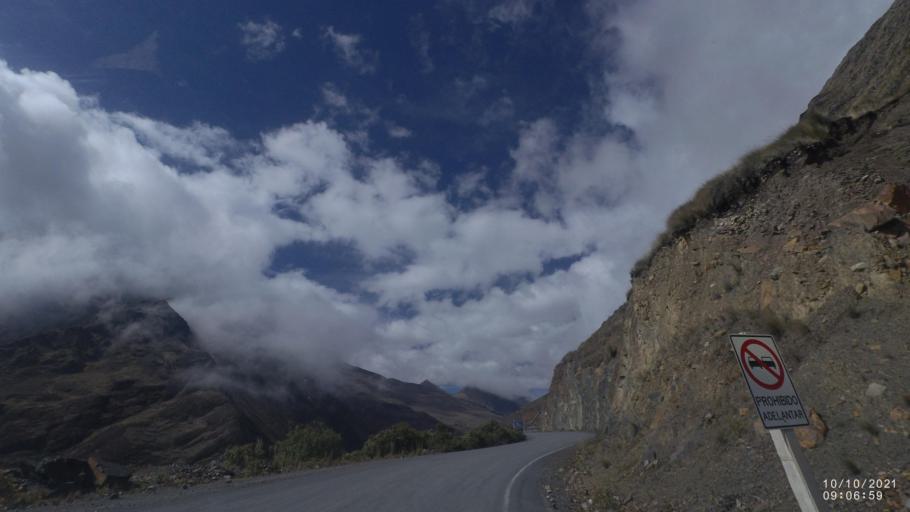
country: BO
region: La Paz
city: Quime
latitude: -17.0070
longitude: -67.2739
